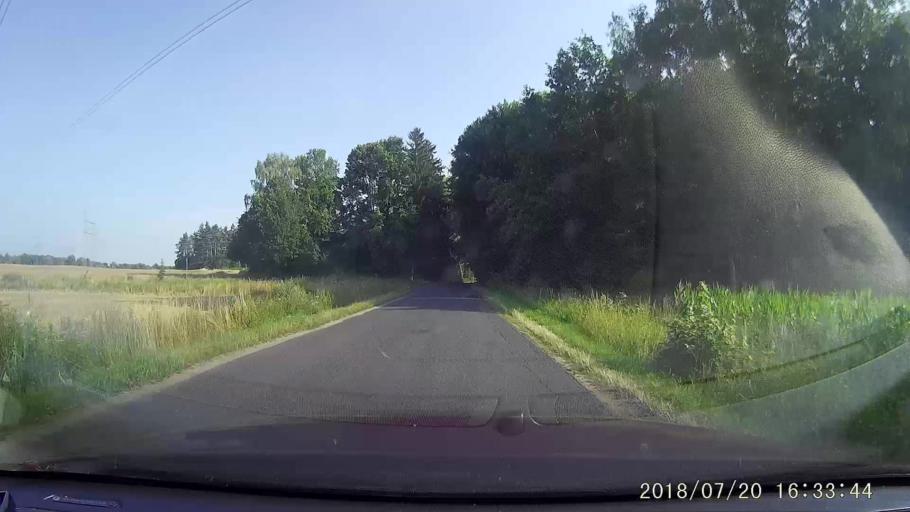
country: PL
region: Lower Silesian Voivodeship
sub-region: Powiat zgorzelecki
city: Sulikow
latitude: 51.0874
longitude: 15.0974
